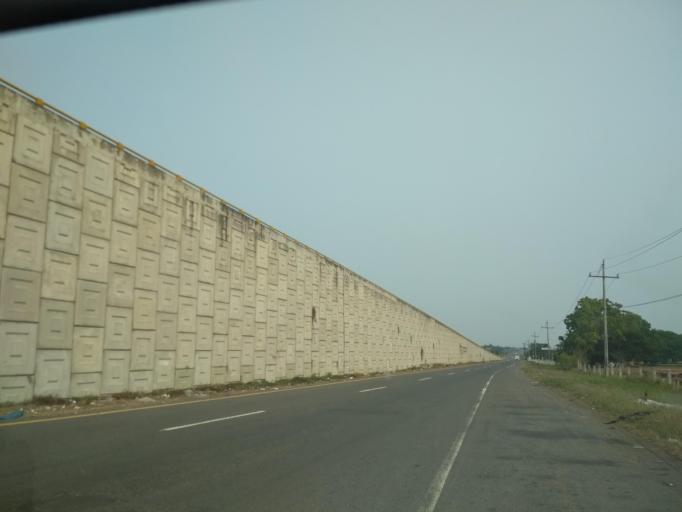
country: MX
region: Veracruz
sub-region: Veracruz
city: Delfino Victoria (Santa Fe)
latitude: 19.1877
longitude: -96.2745
